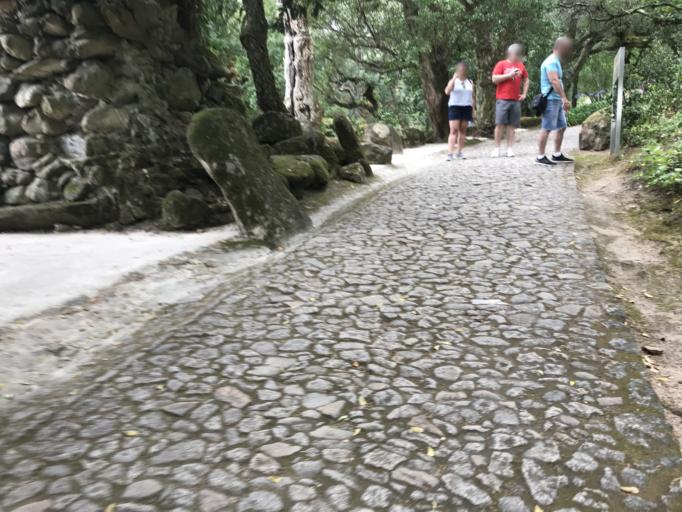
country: PT
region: Lisbon
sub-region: Sintra
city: Colares
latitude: 38.7927
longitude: -9.4194
